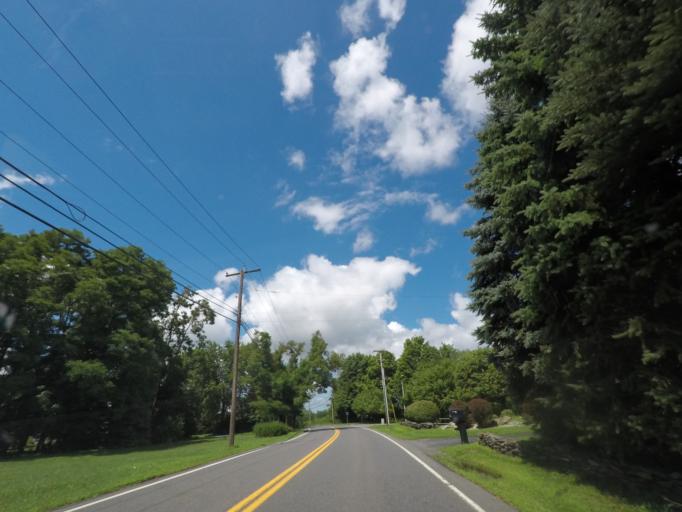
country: US
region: New York
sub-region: Rensselaer County
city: Wynantskill
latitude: 42.6885
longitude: -73.6823
